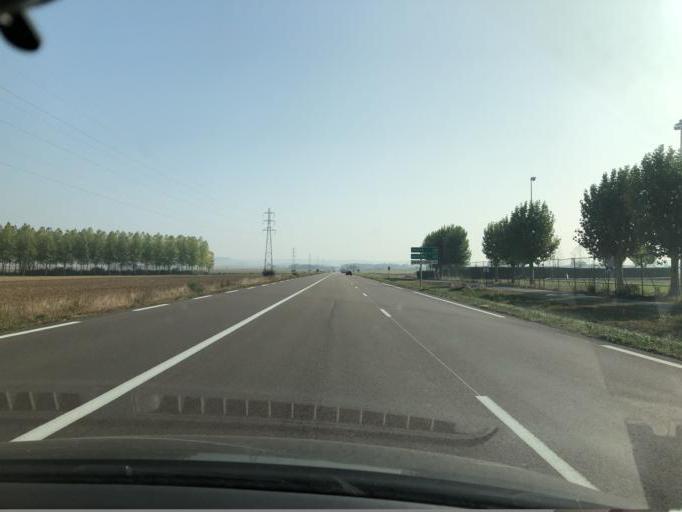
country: FR
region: Bourgogne
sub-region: Departement de l'Yonne
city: Saint-Martin-du-Tertre
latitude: 48.2303
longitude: 3.2702
